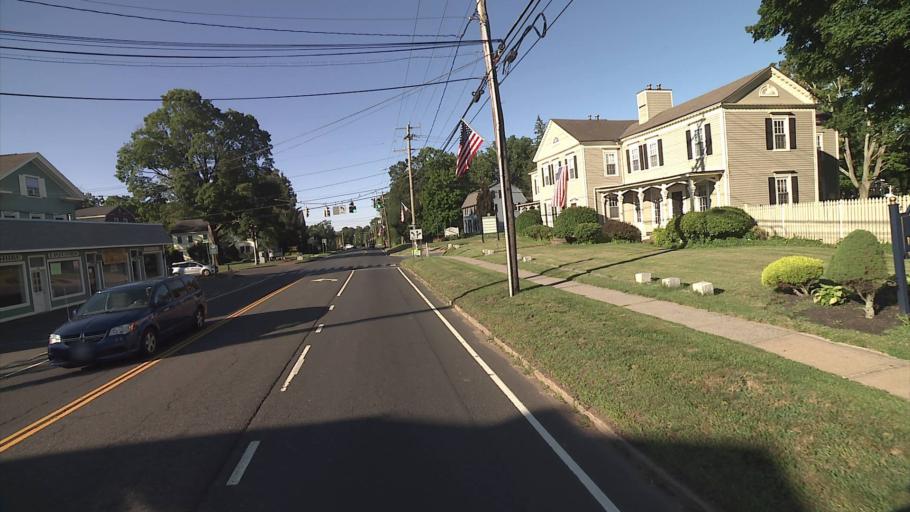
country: US
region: Connecticut
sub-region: New Haven County
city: Cheshire
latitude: 41.4967
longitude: -72.9026
